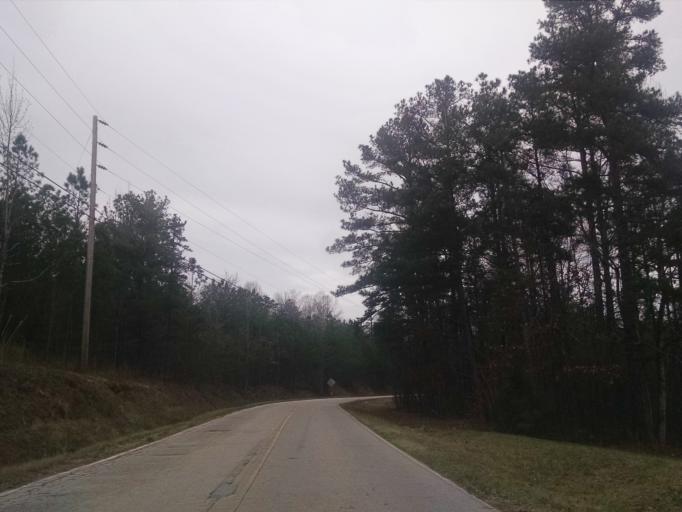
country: US
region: Georgia
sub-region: Hall County
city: Flowery Branch
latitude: 34.1825
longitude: -83.8995
